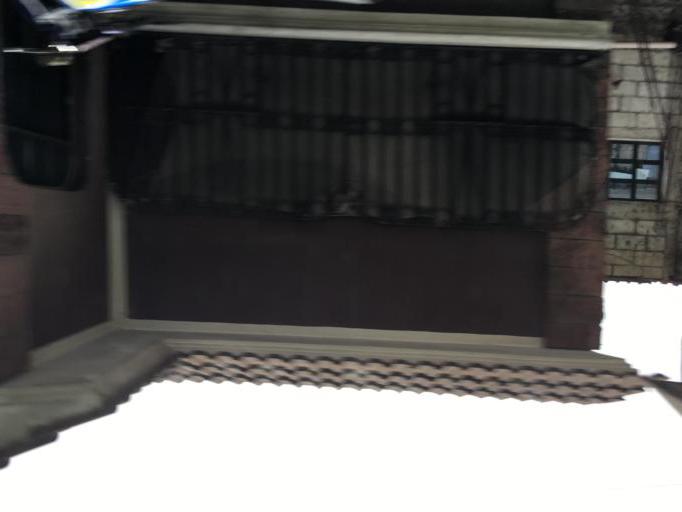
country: GT
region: Guatemala
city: Villa Canales
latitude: 14.4420
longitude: -90.5604
